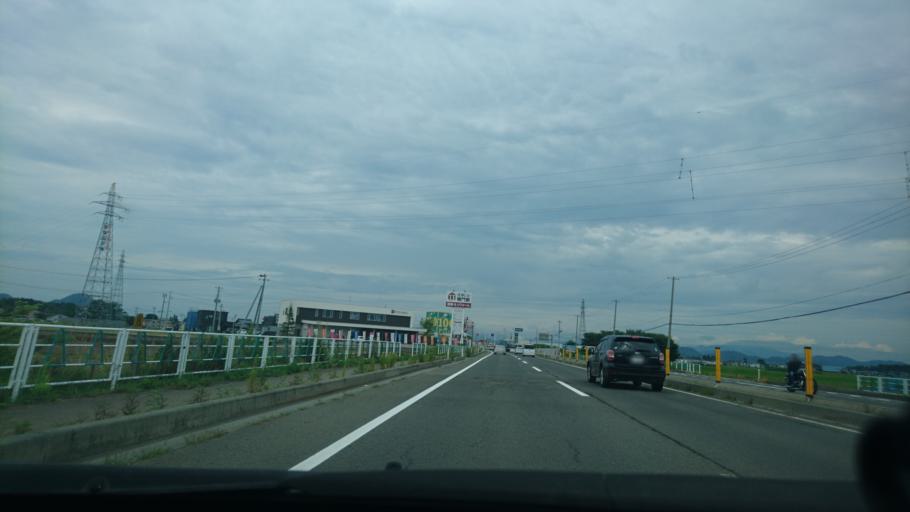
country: JP
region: Akita
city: Omagari
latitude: 39.4516
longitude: 140.5000
